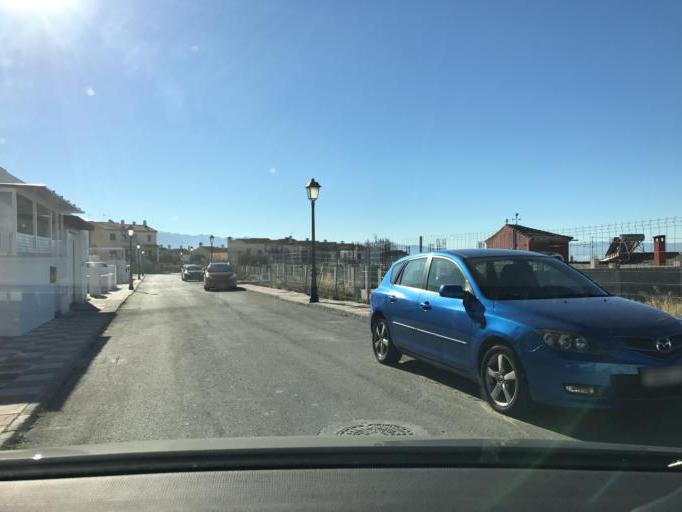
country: ES
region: Andalusia
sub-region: Provincia de Granada
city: Alfacar
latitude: 37.2438
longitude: -3.5666
